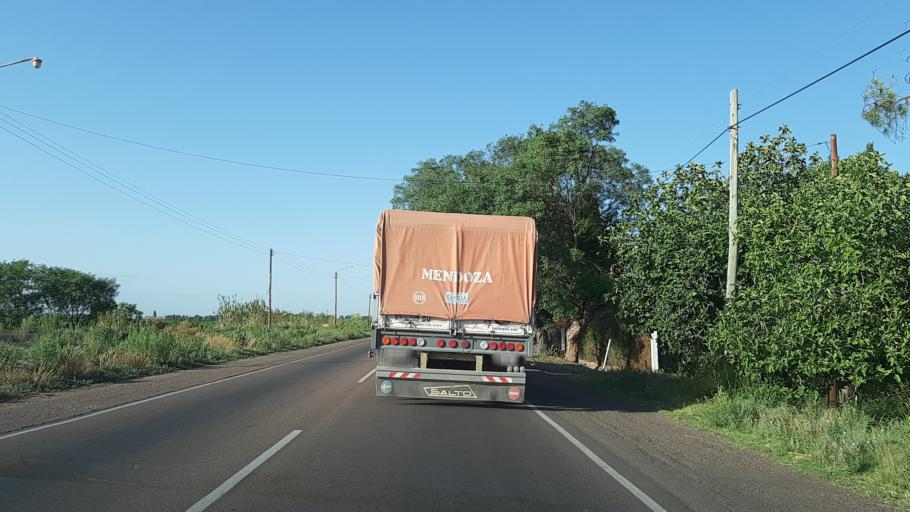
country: AR
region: Mendoza
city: San Martin
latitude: -32.9915
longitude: -68.4704
